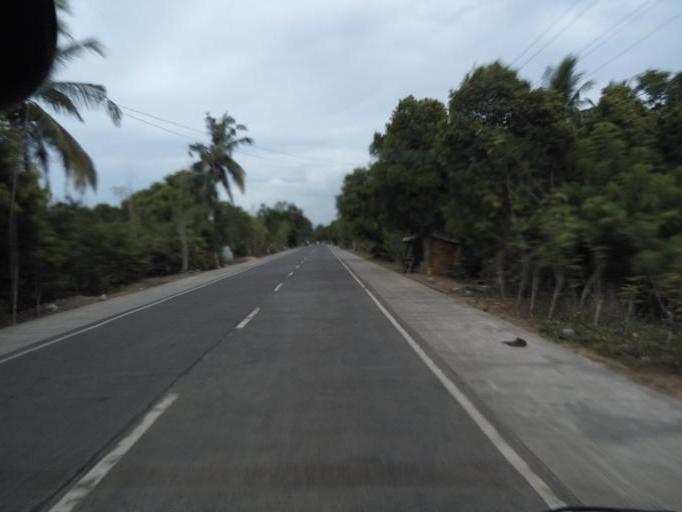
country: PH
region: Cagayan Valley
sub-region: Province of Cagayan
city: Santa Teresita
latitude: 18.2464
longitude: 121.9393
